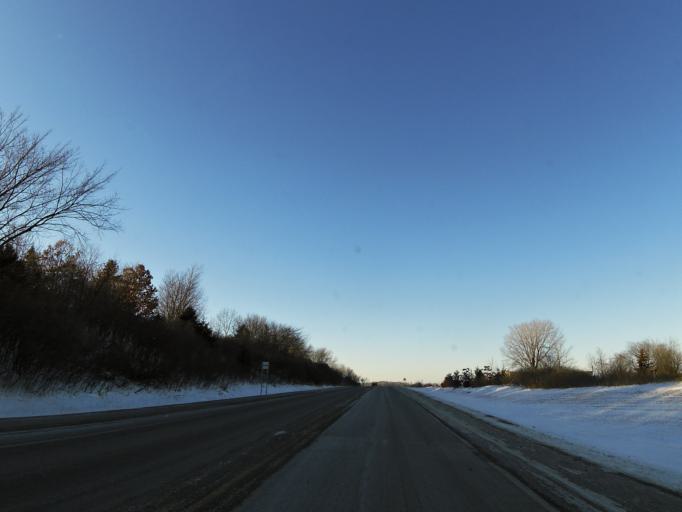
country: US
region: Minnesota
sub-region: Rice County
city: Lonsdale
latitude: 44.4826
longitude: -93.4374
